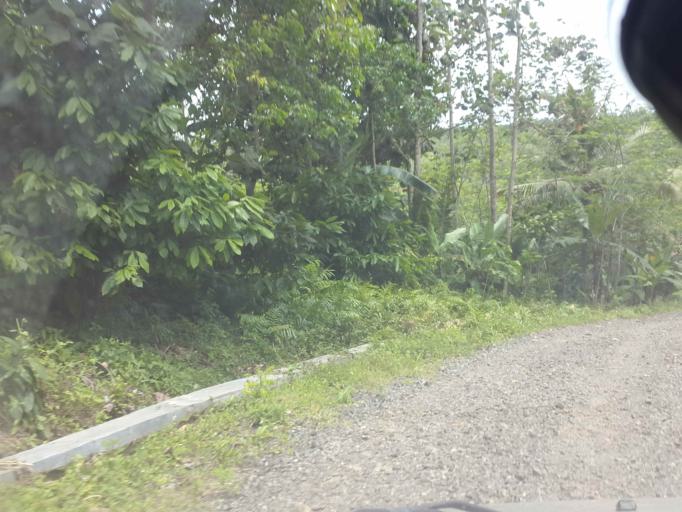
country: ID
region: Lampung
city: Sidorejo
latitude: -5.5619
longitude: 105.4795
